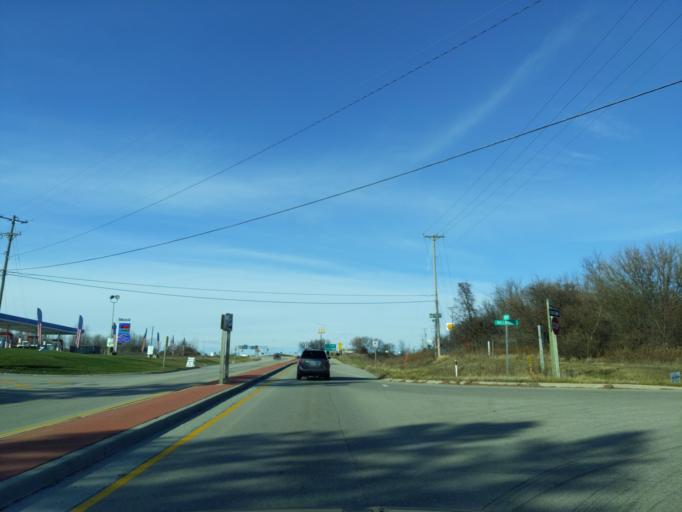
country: US
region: Wisconsin
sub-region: Rock County
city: Edgerton
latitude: 42.8327
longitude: -89.0233
